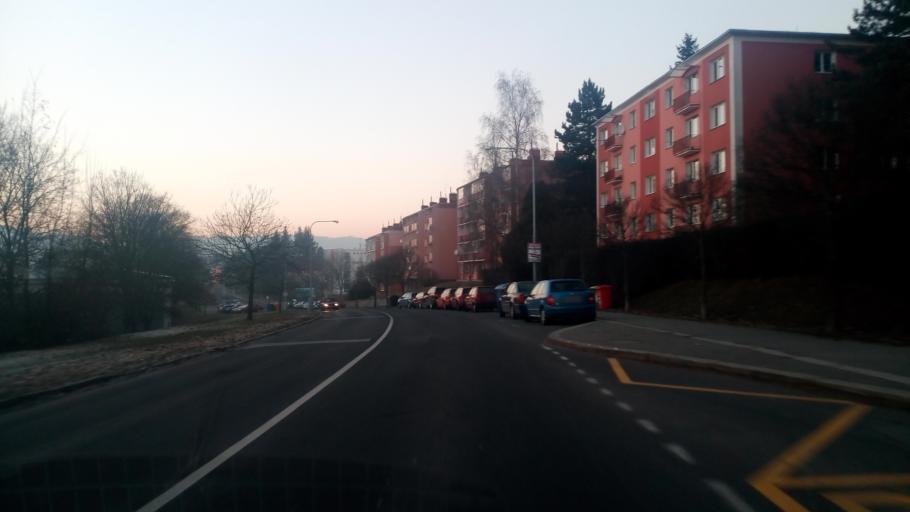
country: CZ
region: Olomoucky
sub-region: Okres Sumperk
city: Sumperk
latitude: 49.9715
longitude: 16.9819
